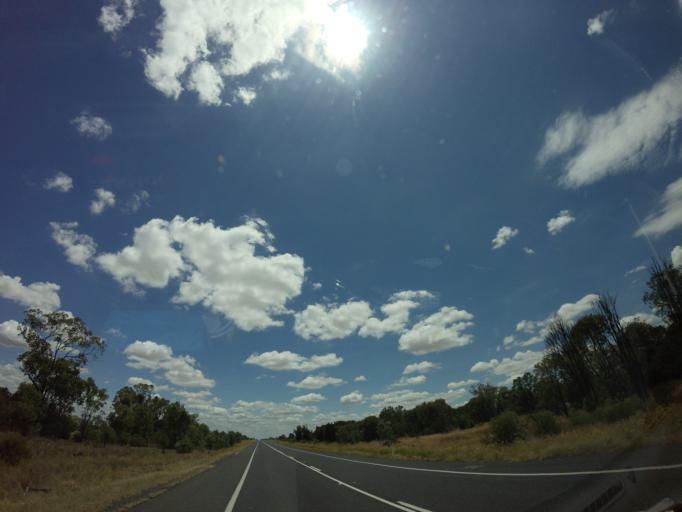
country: AU
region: New South Wales
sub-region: Moree Plains
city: Boggabilla
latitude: -28.8435
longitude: 150.2239
